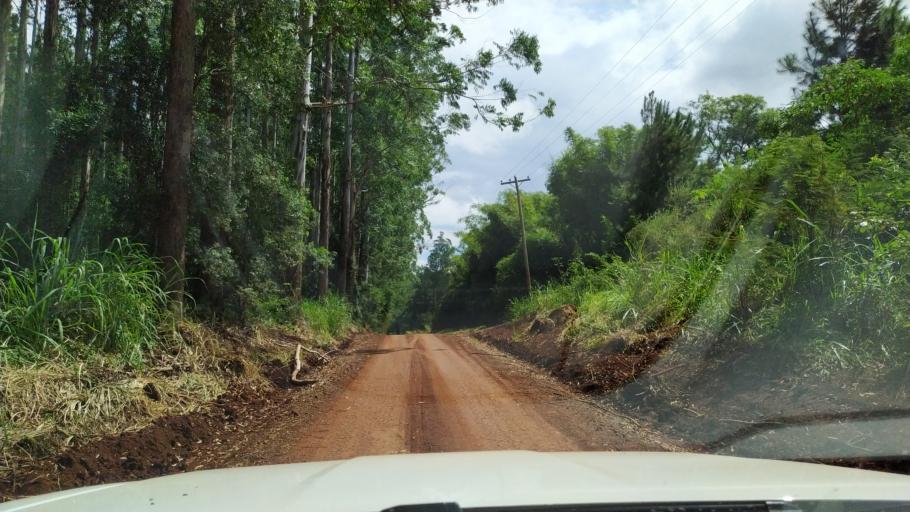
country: AR
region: Misiones
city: Puerto Piray
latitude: -26.5322
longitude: -54.6179
